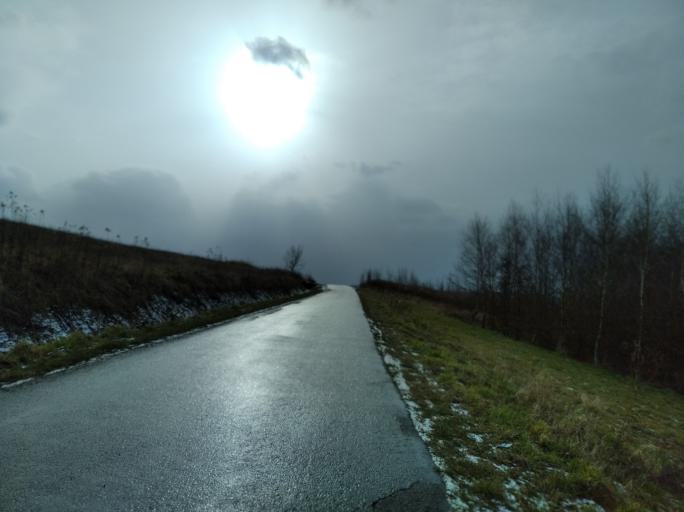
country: PL
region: Subcarpathian Voivodeship
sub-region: Powiat strzyzowski
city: Wysoka Strzyzowska
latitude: 49.8842
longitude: 21.7279
